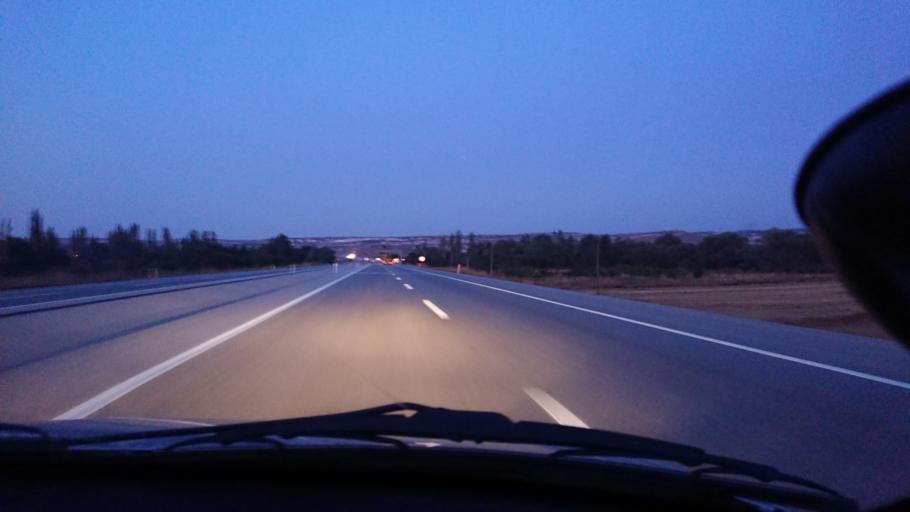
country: TR
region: Kuetahya
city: Cavdarhisar
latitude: 39.1249
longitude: 29.5397
